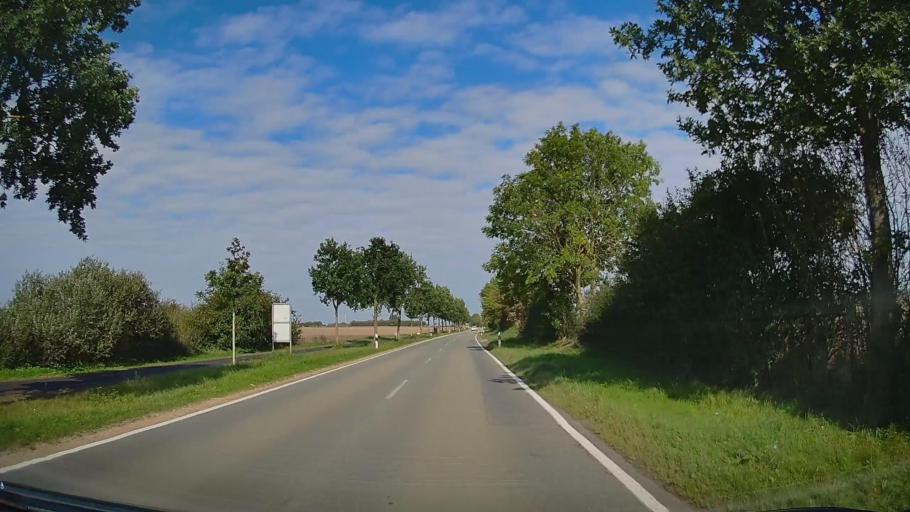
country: DE
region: Schleswig-Holstein
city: Oldenburg in Holstein
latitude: 54.3039
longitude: 10.8872
